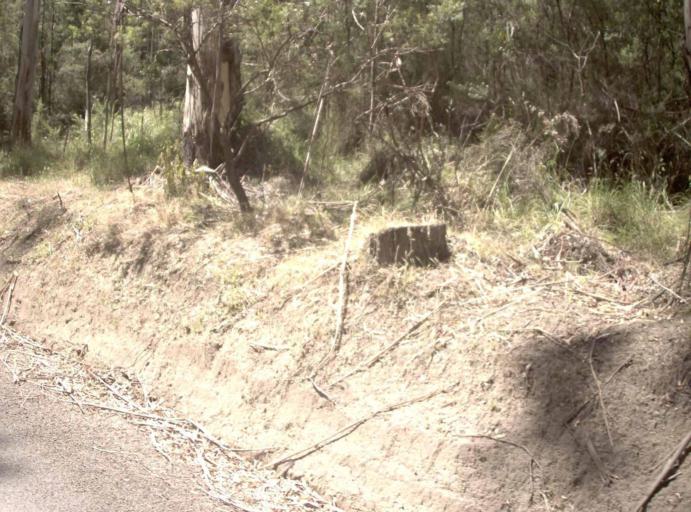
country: AU
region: Victoria
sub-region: Baw Baw
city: Warragul
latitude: -37.8317
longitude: 145.9965
